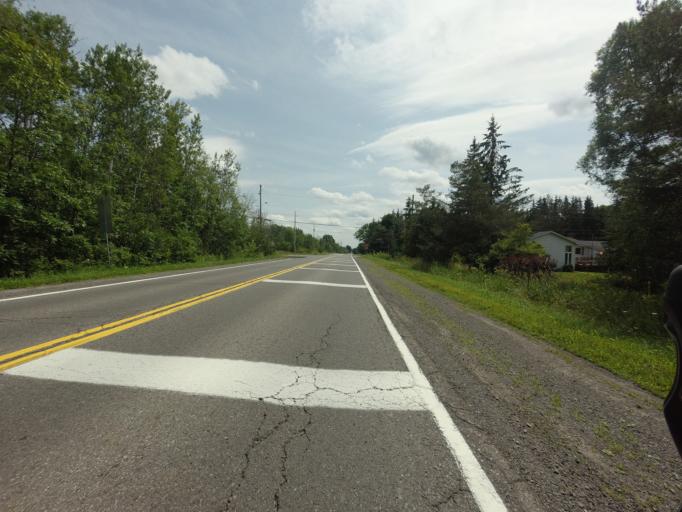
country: CA
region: Ontario
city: Ottawa
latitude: 45.2772
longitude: -75.6265
